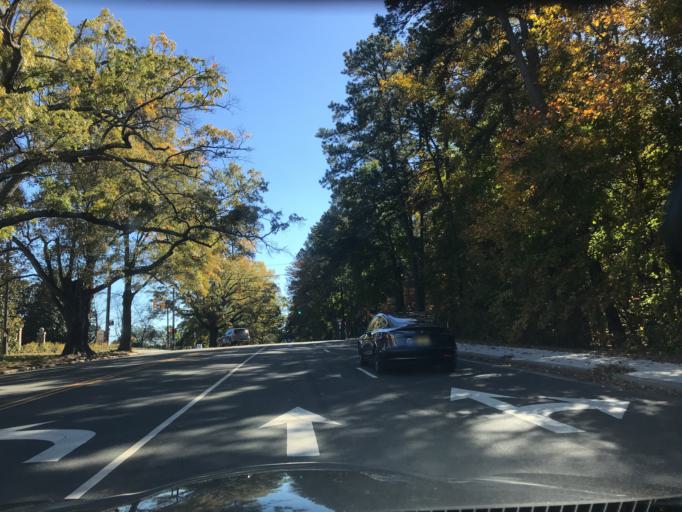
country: US
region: North Carolina
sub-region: Durham County
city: Durham
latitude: 35.9956
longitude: -78.9478
